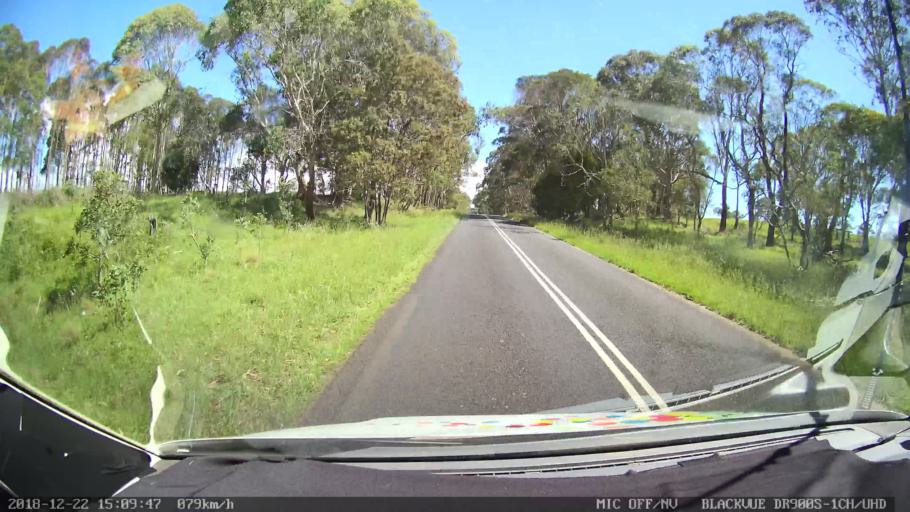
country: AU
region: New South Wales
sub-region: Bellingen
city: Dorrigo
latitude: -30.3274
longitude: 152.4063
